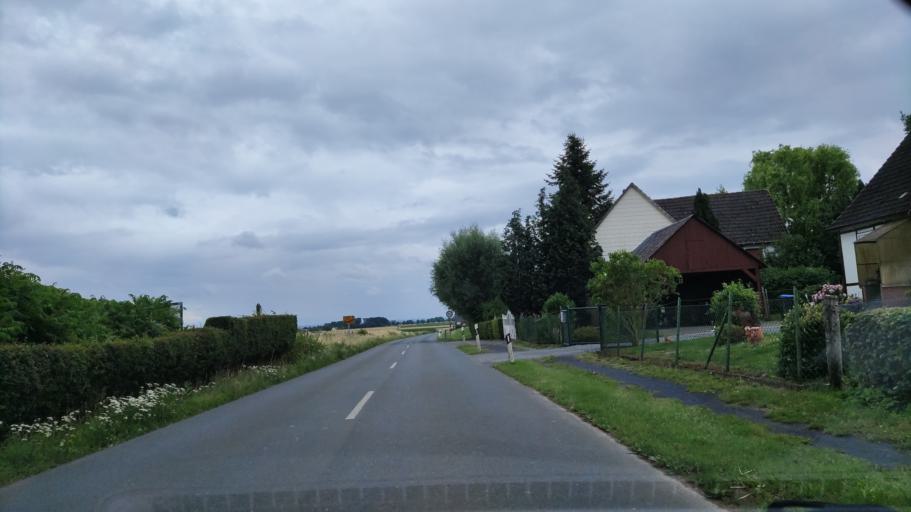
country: DE
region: North Rhine-Westphalia
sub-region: Regierungsbezirk Arnsberg
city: Soest
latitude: 51.6039
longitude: 8.0479
